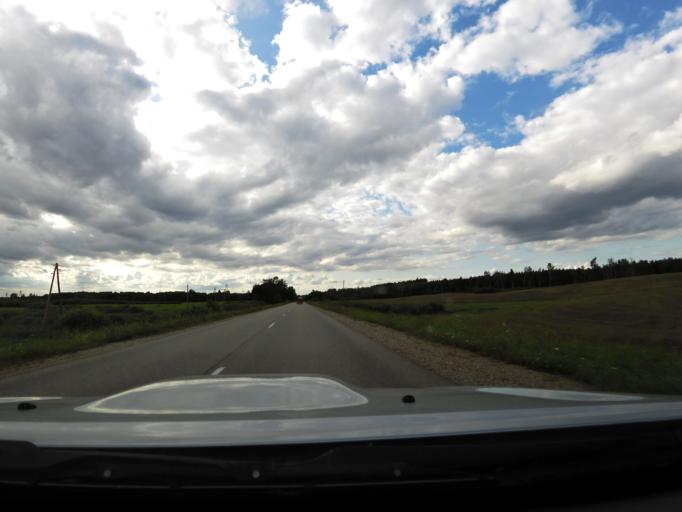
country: LV
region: Ilukste
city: Ilukste
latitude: 55.9653
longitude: 26.0434
